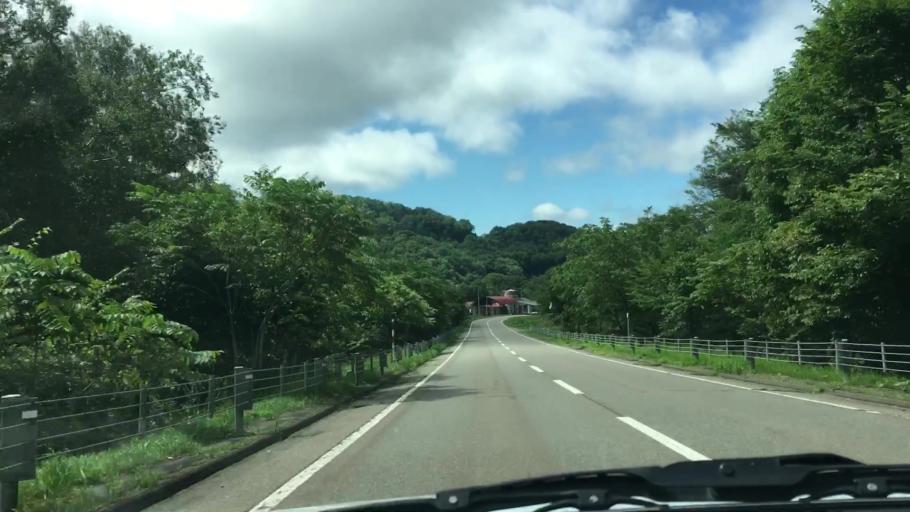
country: JP
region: Hokkaido
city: Kitami
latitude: 43.3541
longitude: 143.8008
